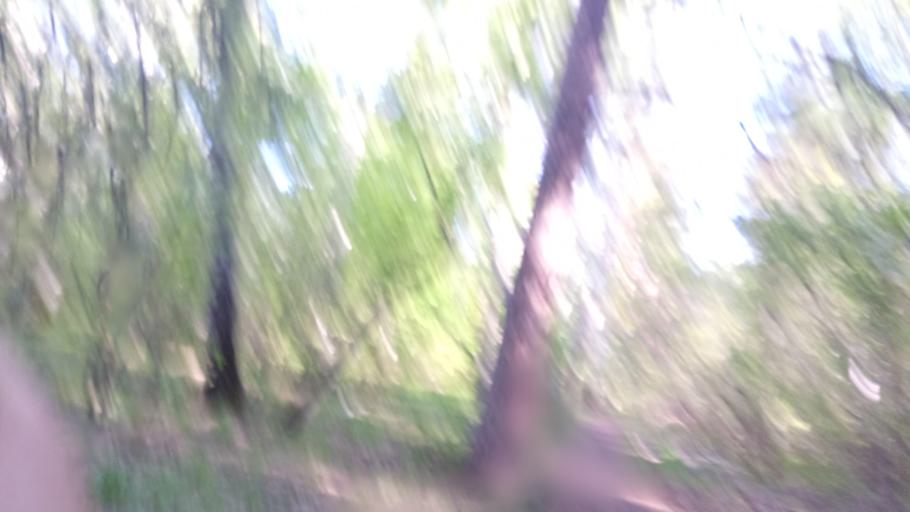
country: RU
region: Chelyabinsk
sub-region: Gorod Chelyabinsk
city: Chelyabinsk
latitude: 55.1424
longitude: 61.3395
